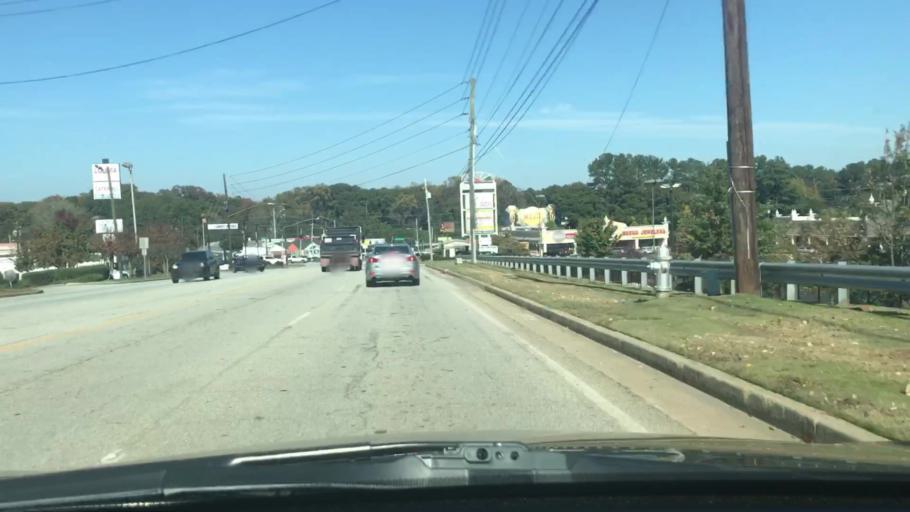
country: US
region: Georgia
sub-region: DeKalb County
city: Scottdale
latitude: 33.7968
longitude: -84.2823
